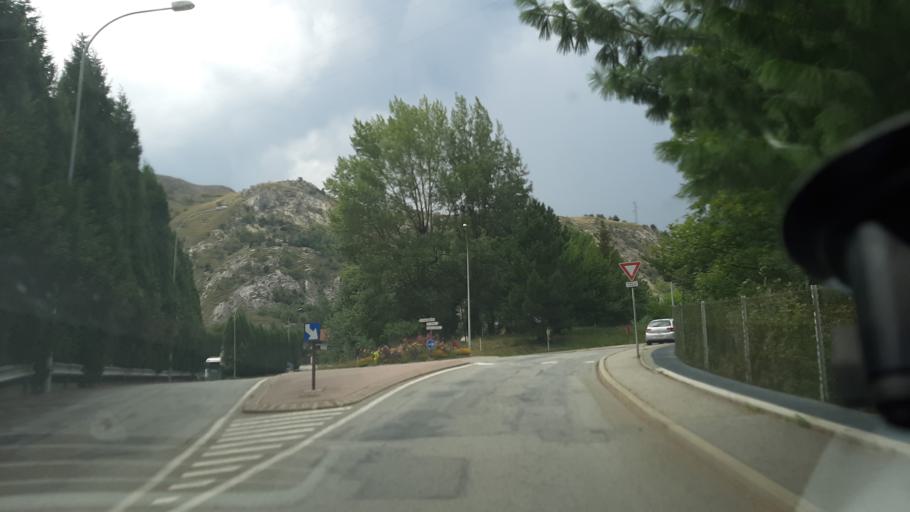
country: FR
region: Rhone-Alpes
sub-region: Departement de la Savoie
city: Saint-Michel-de-Maurienne
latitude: 45.2228
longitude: 6.4639
